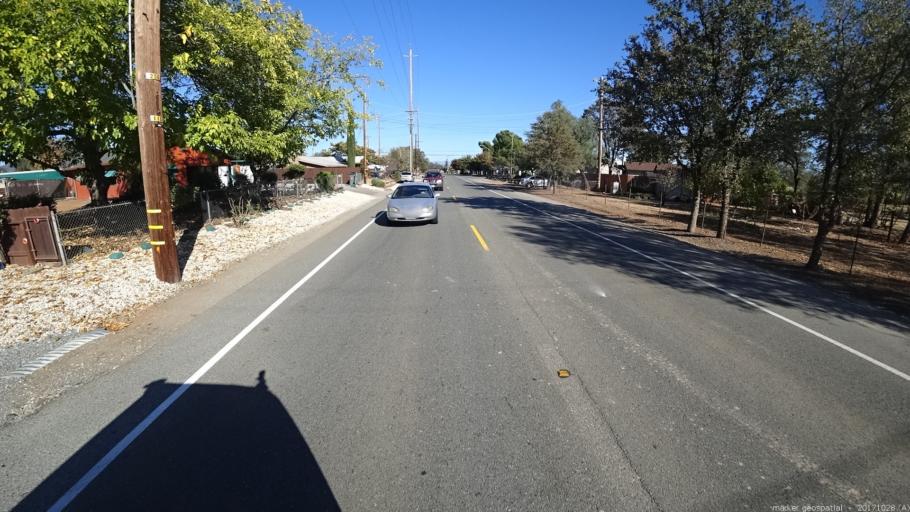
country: US
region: California
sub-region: Shasta County
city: Redding
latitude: 40.6323
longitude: -122.3935
